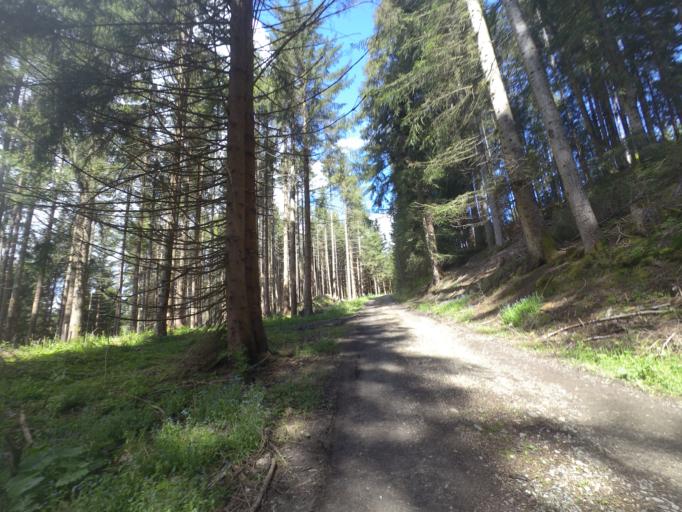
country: AT
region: Salzburg
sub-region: Politischer Bezirk Zell am See
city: Lend
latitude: 47.3074
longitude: 13.0562
